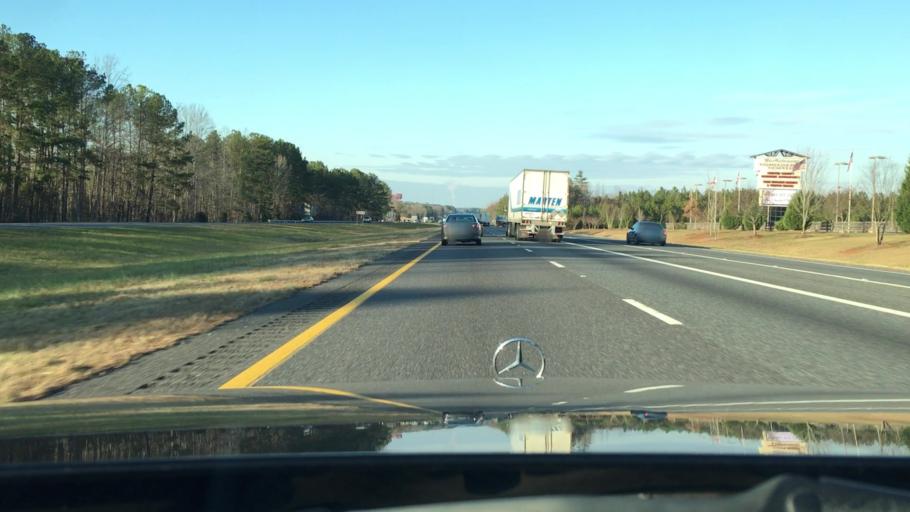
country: US
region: South Carolina
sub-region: Chester County
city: Eureka Mill
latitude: 34.7488
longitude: -81.0356
